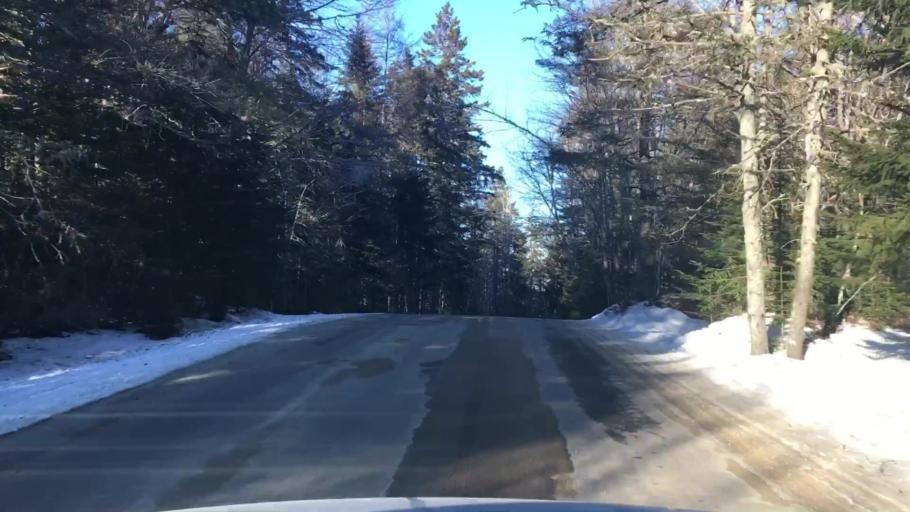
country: US
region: Maine
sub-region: Hancock County
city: Castine
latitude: 44.3837
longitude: -68.7453
